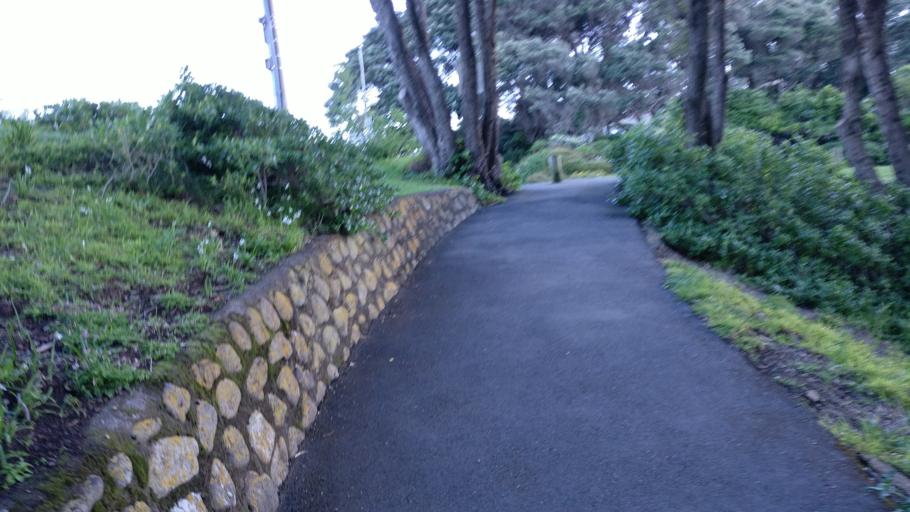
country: NZ
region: Wellington
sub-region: Kapiti Coast District
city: Paraparaumu
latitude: -40.9807
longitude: 174.9570
